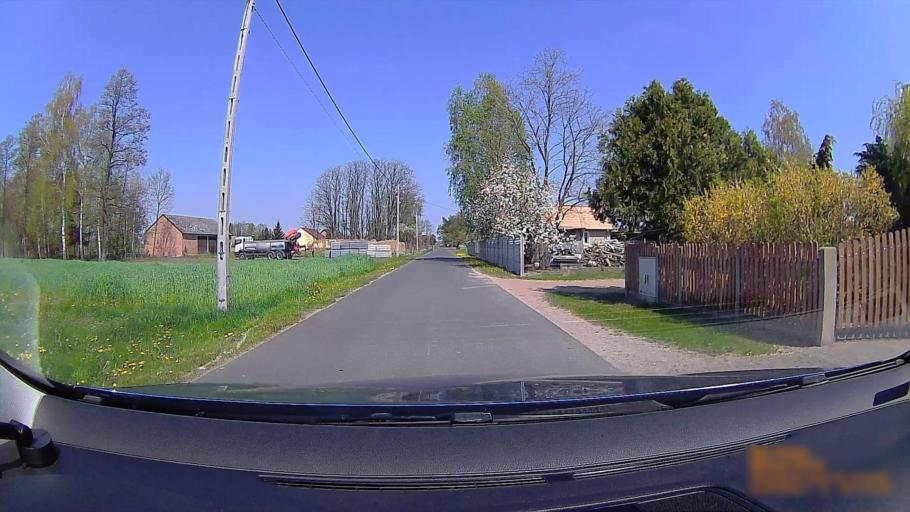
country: PL
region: Greater Poland Voivodeship
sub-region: Powiat koninski
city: Rychwal
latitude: 52.0976
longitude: 18.1841
